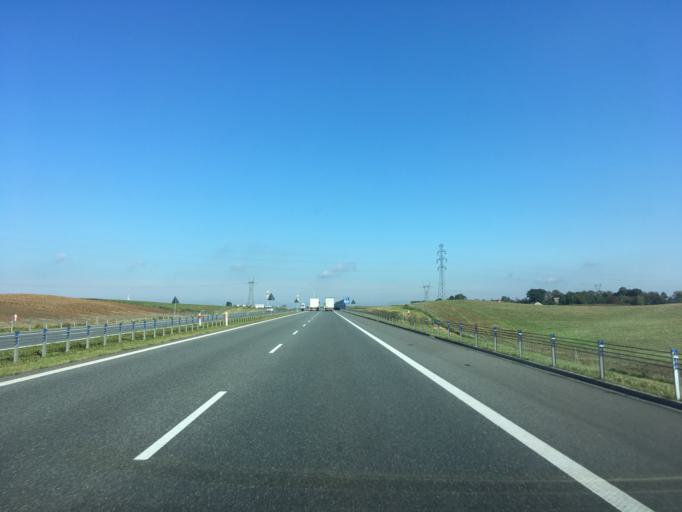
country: PL
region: Kujawsko-Pomorskie
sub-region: Powiat chelminski
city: Lisewo
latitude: 53.3306
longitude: 18.7084
